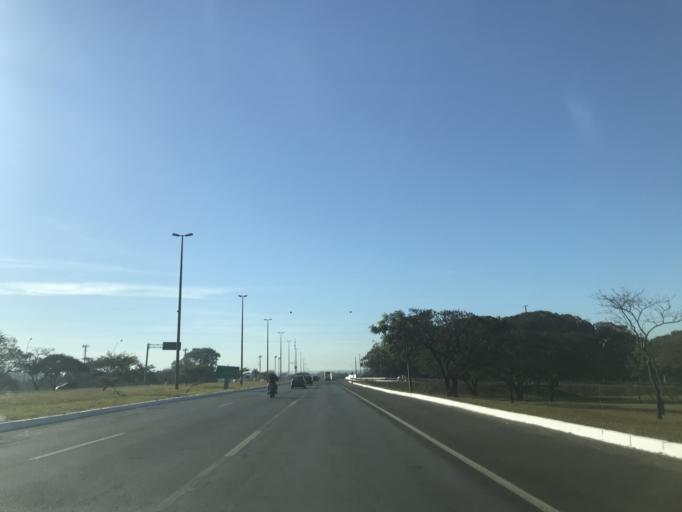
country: BR
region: Federal District
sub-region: Brasilia
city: Brasilia
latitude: -15.8400
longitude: -47.9555
